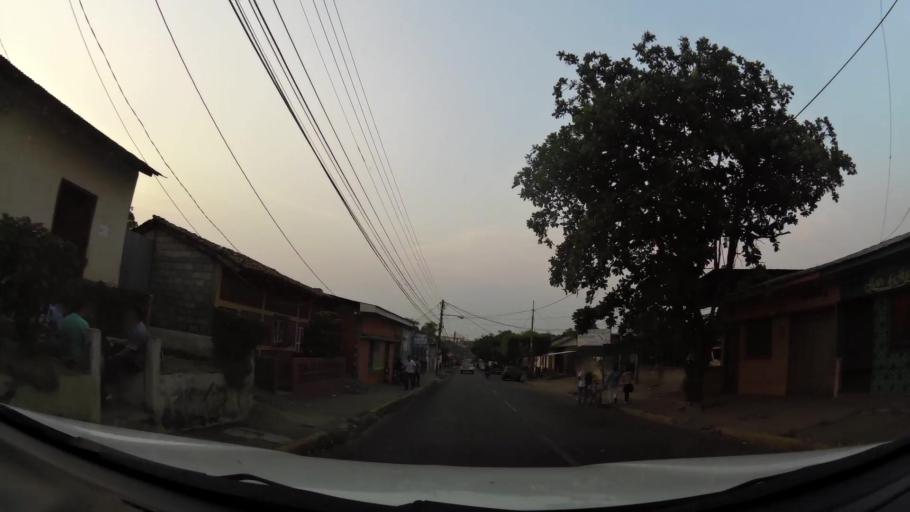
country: NI
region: Leon
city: Leon
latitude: 12.4282
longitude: -86.8766
